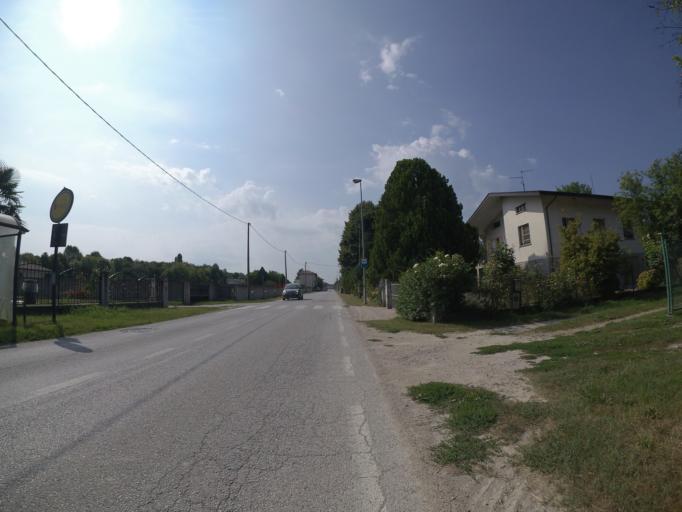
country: IT
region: Friuli Venezia Giulia
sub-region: Provincia di Udine
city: Pocenia
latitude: 45.8266
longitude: 13.0814
